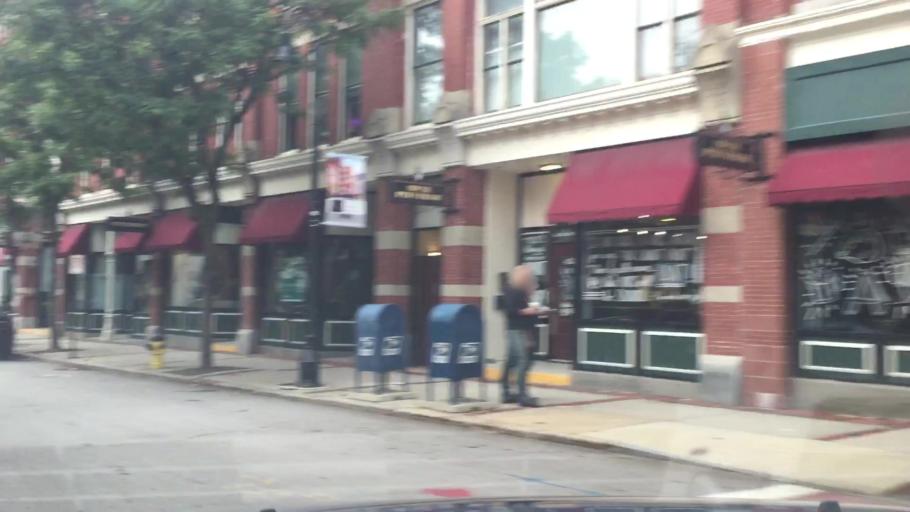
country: US
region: New Hampshire
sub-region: Hillsborough County
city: Manchester
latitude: 42.9905
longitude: -71.4615
